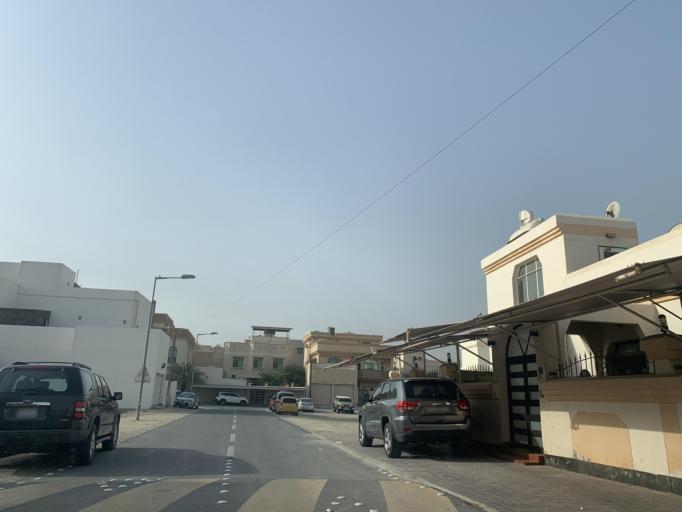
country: BH
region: Northern
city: Madinat `Isa
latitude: 26.1913
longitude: 50.5623
